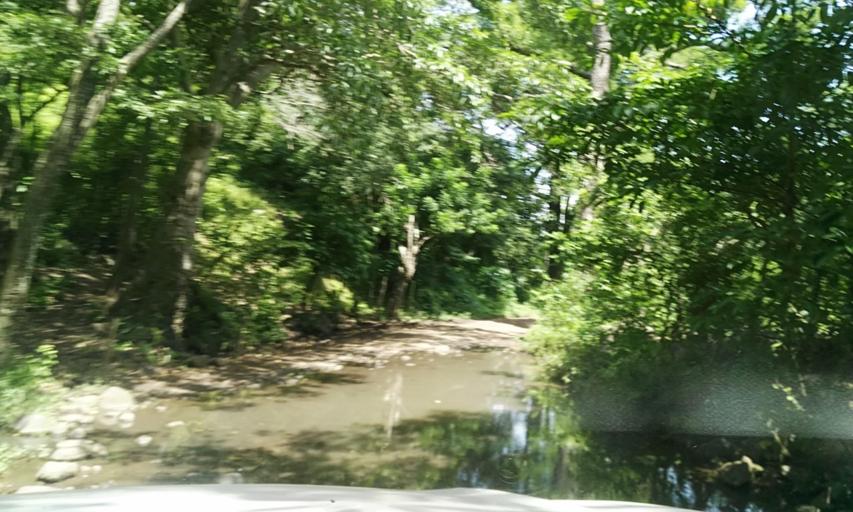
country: NI
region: Matagalpa
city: Terrabona
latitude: 12.7215
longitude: -85.9257
